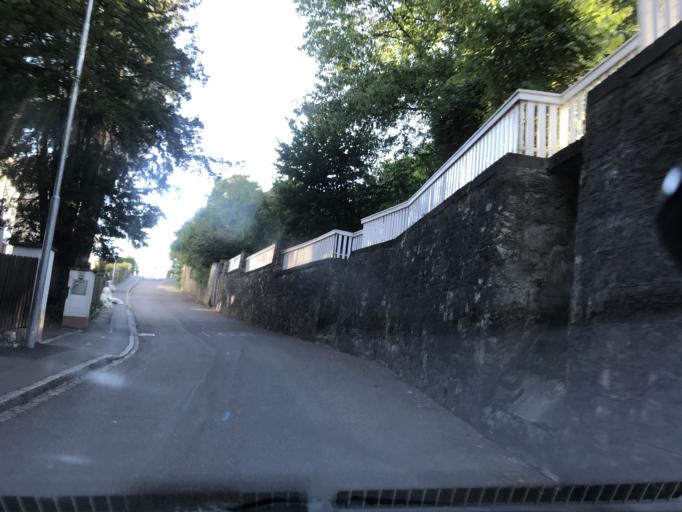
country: DE
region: Baden-Wuerttemberg
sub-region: Freiburg Region
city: Loerrach
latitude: 47.6121
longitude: 7.6675
